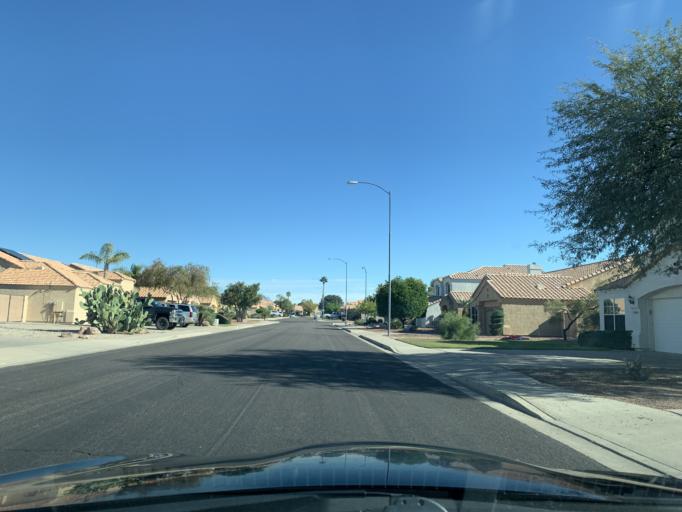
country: US
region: Arizona
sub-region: Pinal County
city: Apache Junction
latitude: 33.3841
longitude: -111.6254
